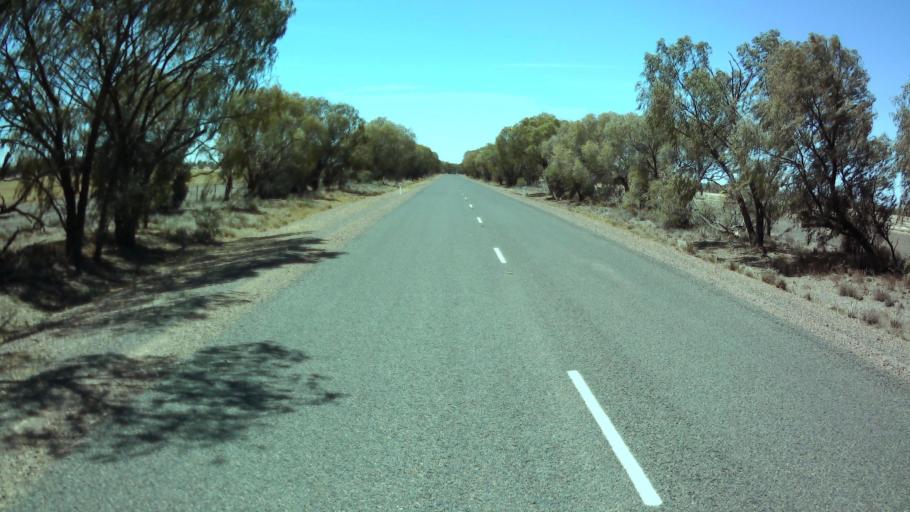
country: AU
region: New South Wales
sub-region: Forbes
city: Forbes
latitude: -33.6625
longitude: 147.6164
